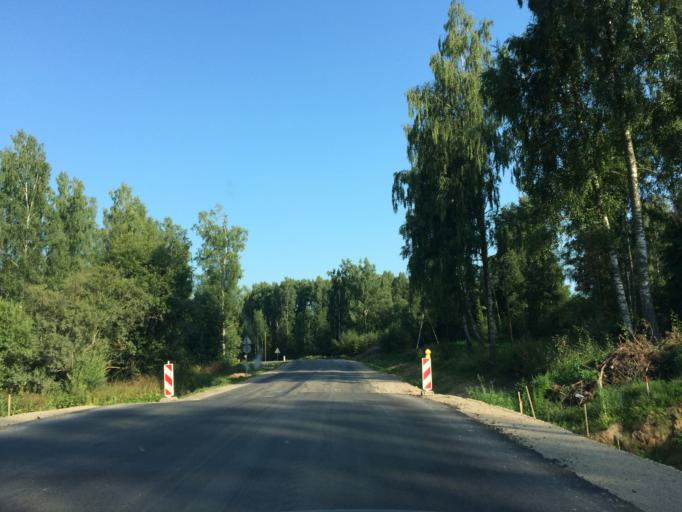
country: LV
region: Rezekne
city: Rezekne
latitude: 56.5142
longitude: 27.4724
